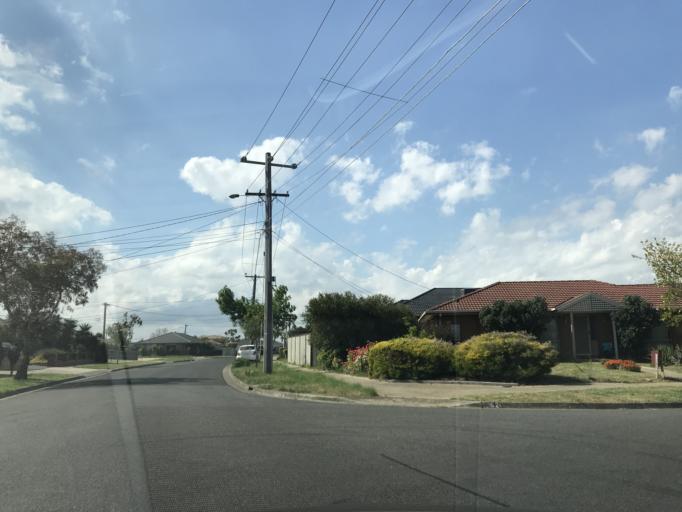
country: AU
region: Victoria
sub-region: Wyndham
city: Hoppers Crossing
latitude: -37.8704
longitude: 144.7155
